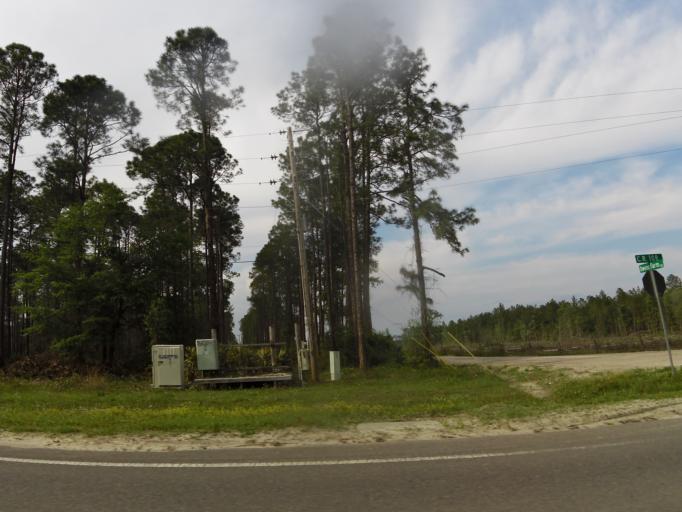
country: US
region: Georgia
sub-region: Camden County
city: Kingsland
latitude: 30.6961
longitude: -81.7283
